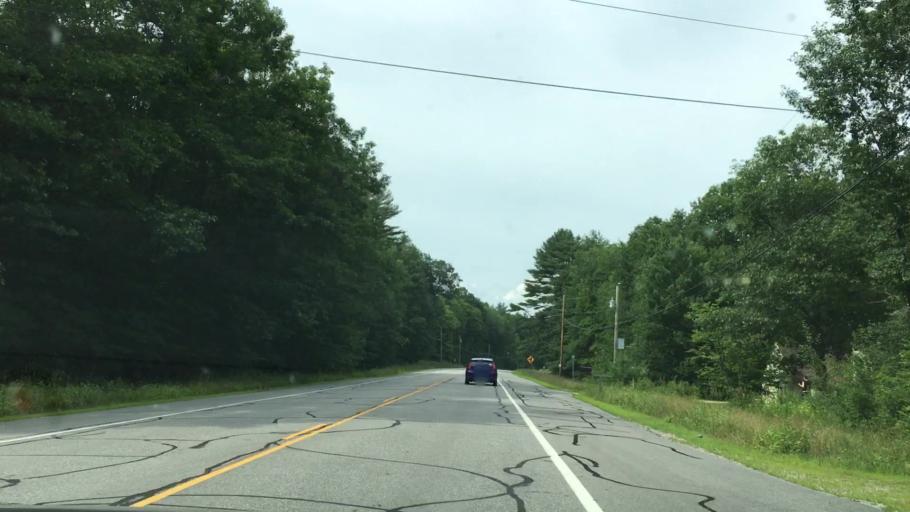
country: US
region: New Hampshire
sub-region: Hillsborough County
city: Hillsborough
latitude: 43.0894
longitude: -71.9194
